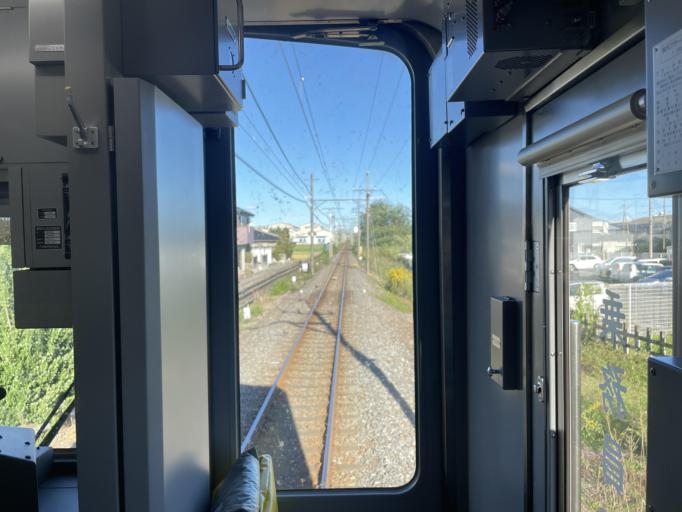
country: JP
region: Tochigi
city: Tochigi
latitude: 36.4021
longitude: 139.7554
